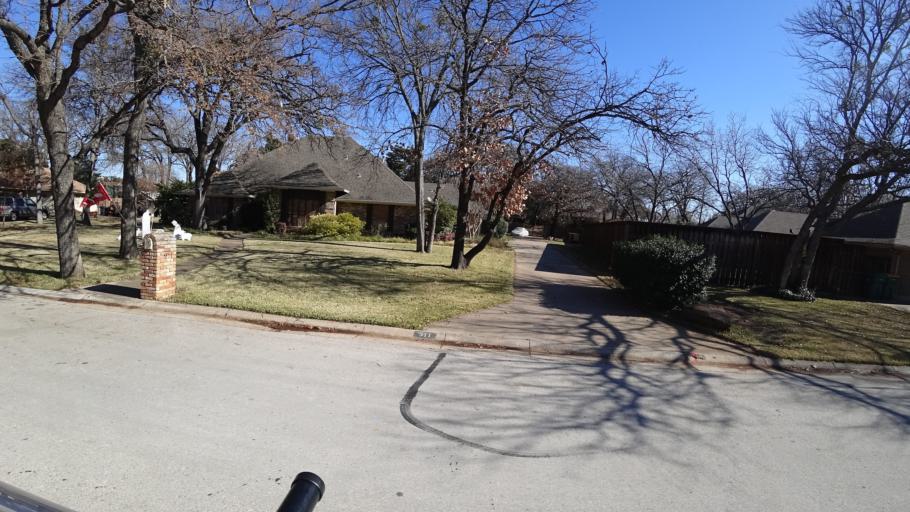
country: US
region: Texas
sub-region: Denton County
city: Lewisville
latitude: 33.0214
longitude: -97.0128
